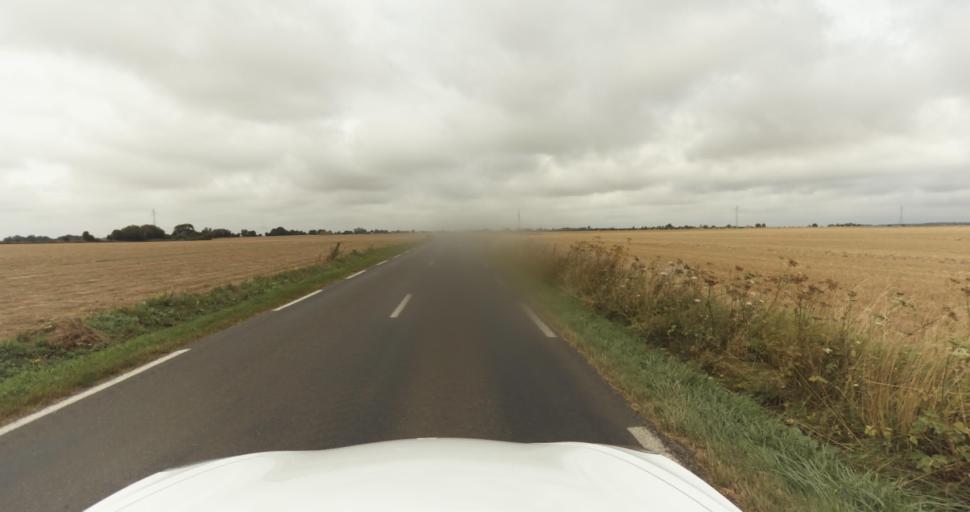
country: FR
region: Haute-Normandie
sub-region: Departement de l'Eure
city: Claville
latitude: 49.0795
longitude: 1.0571
